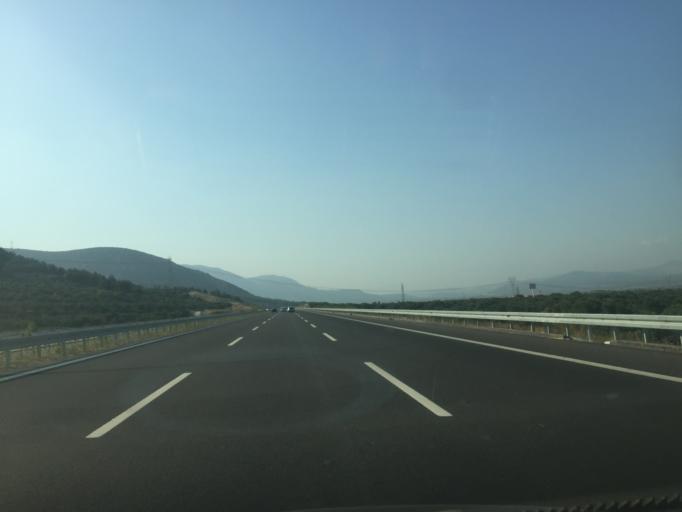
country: TR
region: Manisa
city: Kirkagac
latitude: 39.0544
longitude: 27.7296
